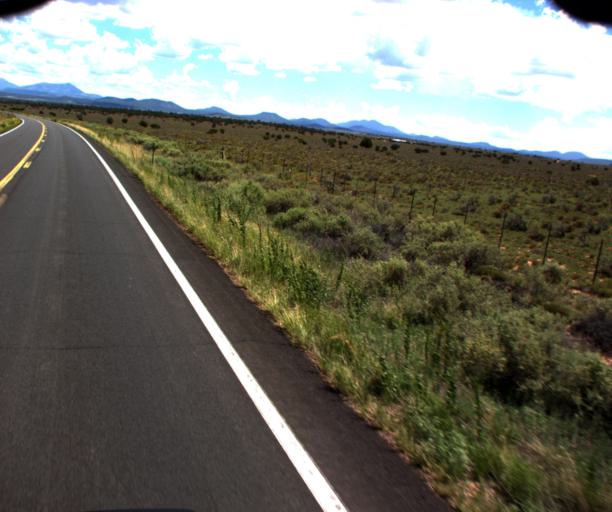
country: US
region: Arizona
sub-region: Coconino County
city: Williams
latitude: 35.6255
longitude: -112.1126
